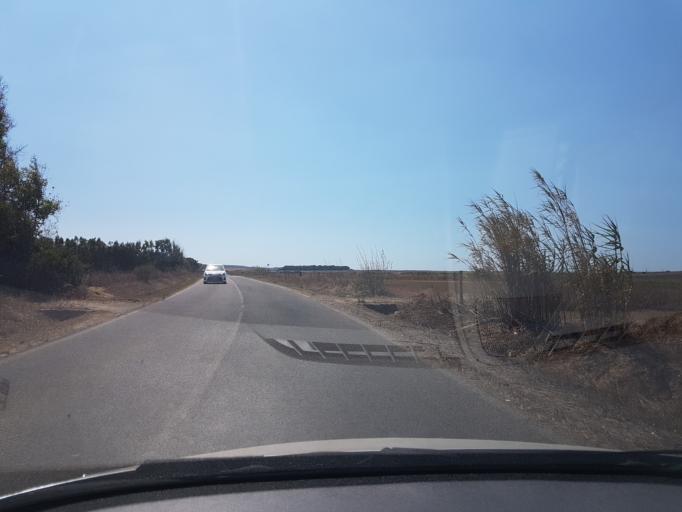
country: IT
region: Sardinia
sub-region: Provincia di Oristano
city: Riola Sardo
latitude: 39.9921
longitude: 8.4642
